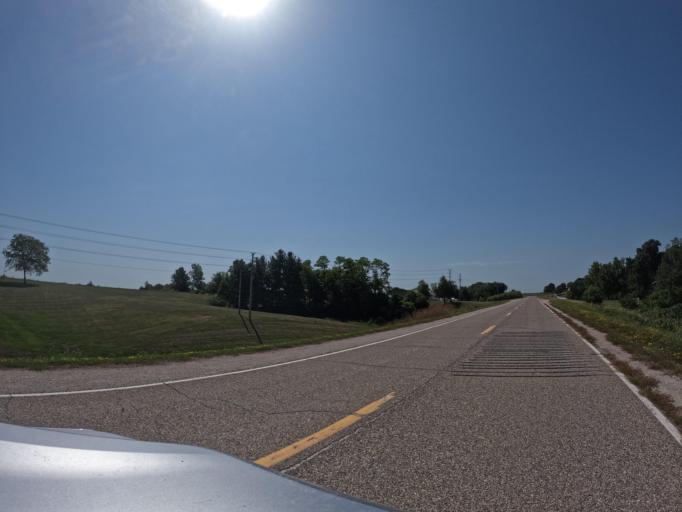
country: US
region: Iowa
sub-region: Henry County
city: Mount Pleasant
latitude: 40.9346
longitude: -91.5403
